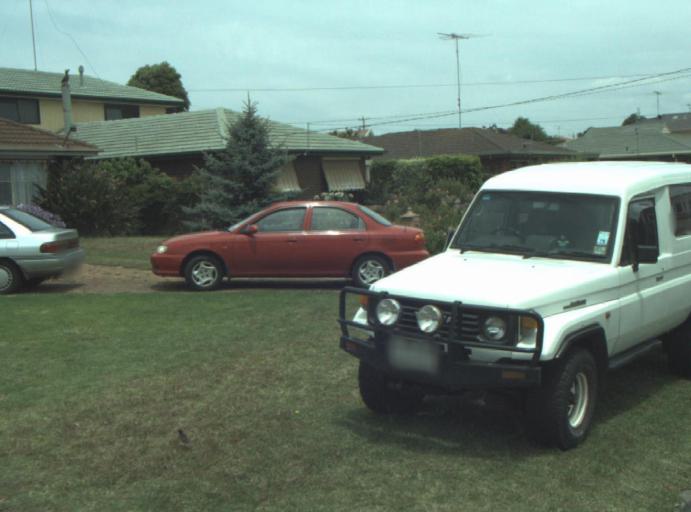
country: AU
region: Victoria
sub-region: Greater Geelong
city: Clifton Springs
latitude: -38.1569
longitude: 144.5547
